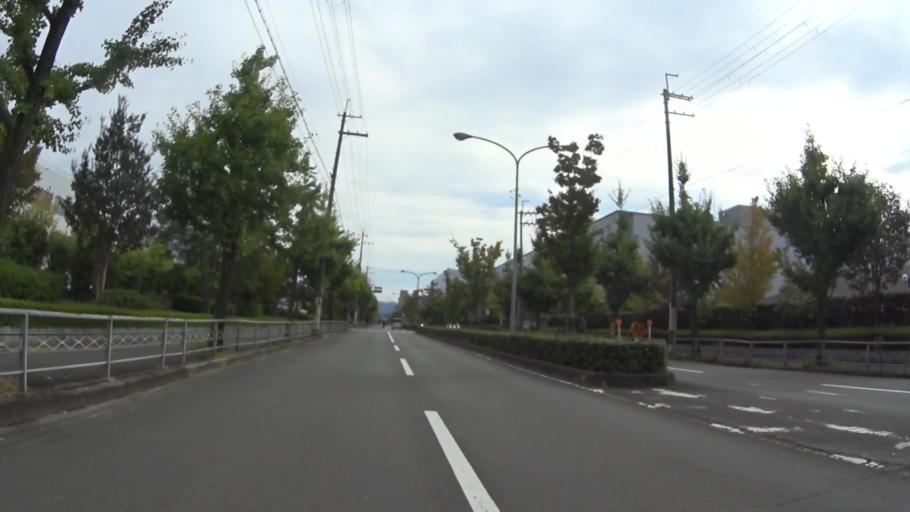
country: JP
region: Kyoto
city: Kyoto
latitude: 35.0109
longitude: 135.7256
